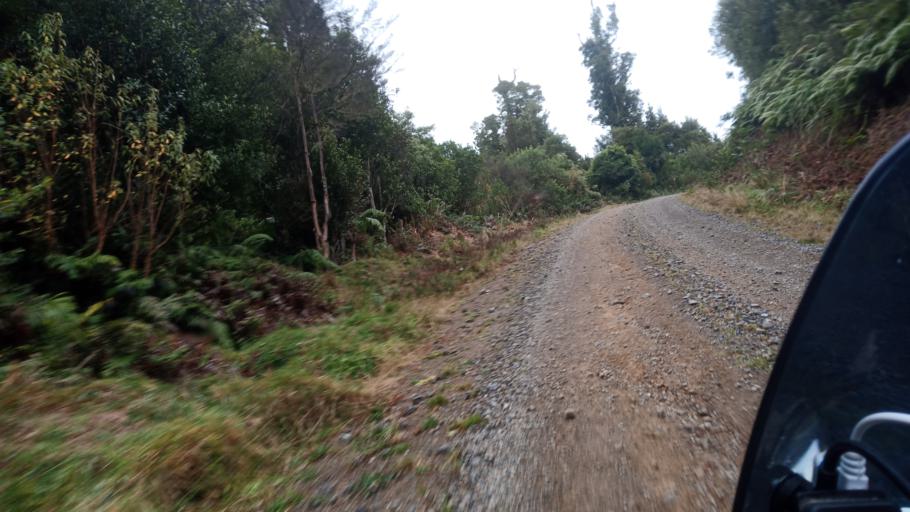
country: NZ
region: Bay of Plenty
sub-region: Whakatane District
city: Murupara
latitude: -38.6755
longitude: 176.6147
